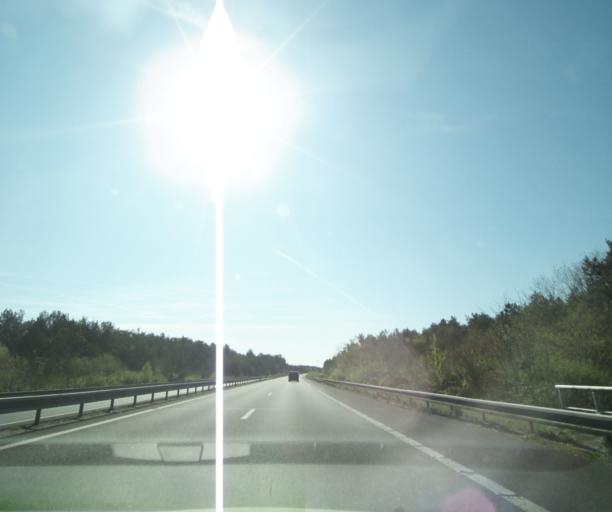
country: FR
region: Centre
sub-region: Departement du Loir-et-Cher
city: Lamotte-Beuvron
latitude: 47.5964
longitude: 1.9820
